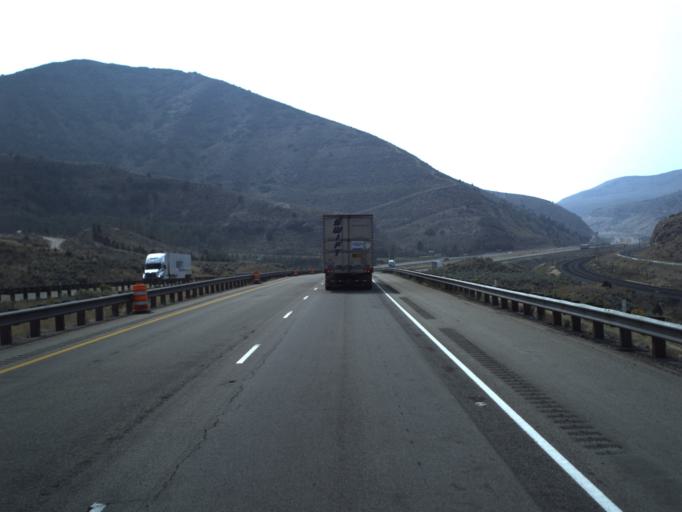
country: US
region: Utah
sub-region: Summit County
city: Coalville
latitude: 41.0486
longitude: -111.3013
